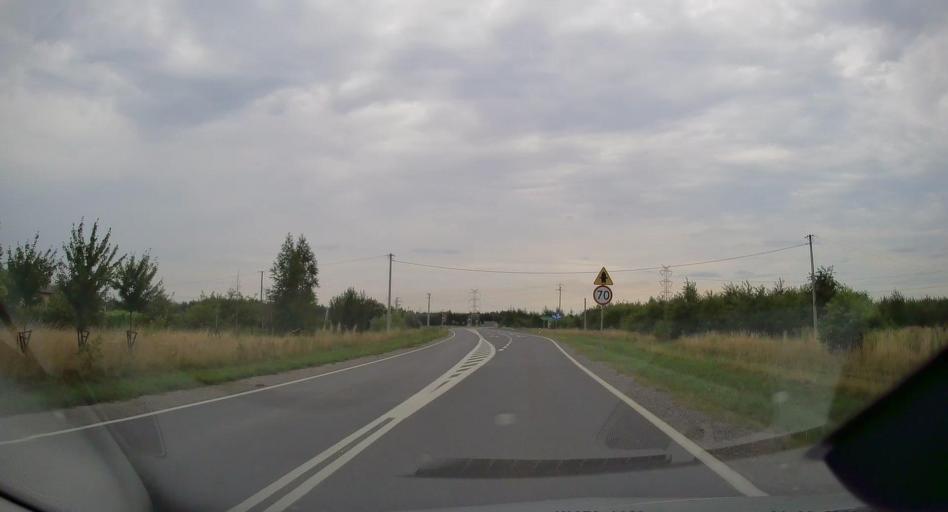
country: PL
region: Lesser Poland Voivodeship
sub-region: Powiat tarnowski
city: Wojnicz
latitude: 49.9794
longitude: 20.8414
